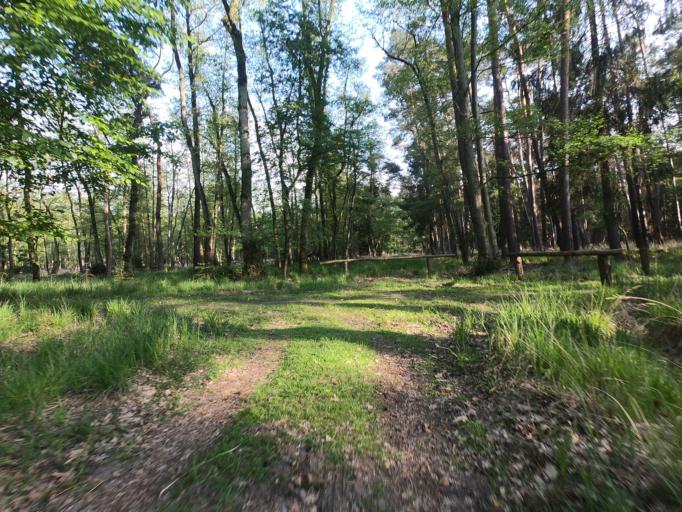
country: DE
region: Hesse
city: Morfelden-Walldorf
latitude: 50.0040
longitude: 8.5433
